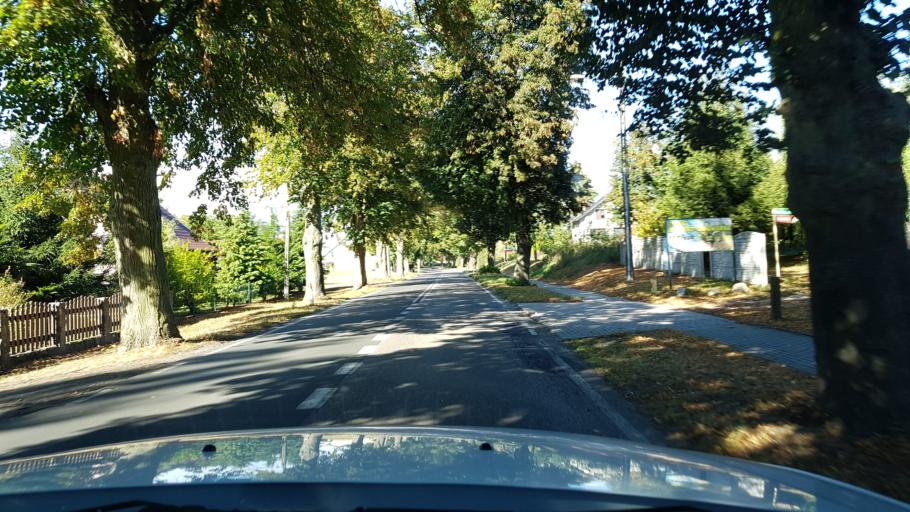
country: PL
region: West Pomeranian Voivodeship
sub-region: Powiat gryfinski
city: Gryfino
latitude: 53.2090
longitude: 14.5011
